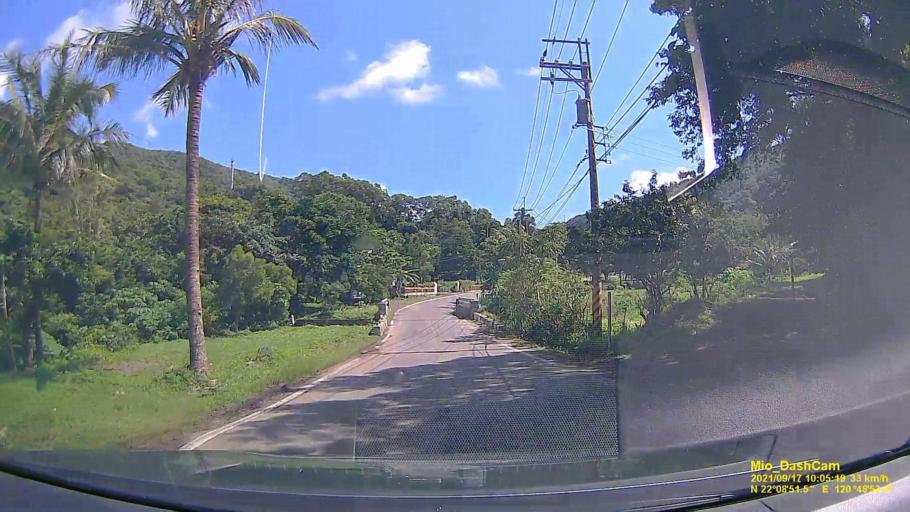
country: TW
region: Taiwan
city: Hengchun
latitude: 22.1477
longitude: 120.8150
